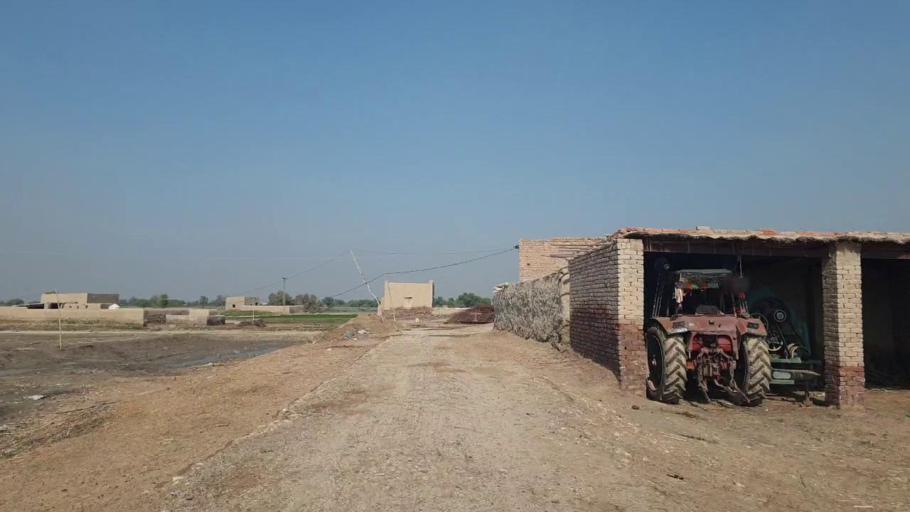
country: PK
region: Sindh
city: Sehwan
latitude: 26.4246
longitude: 67.8103
